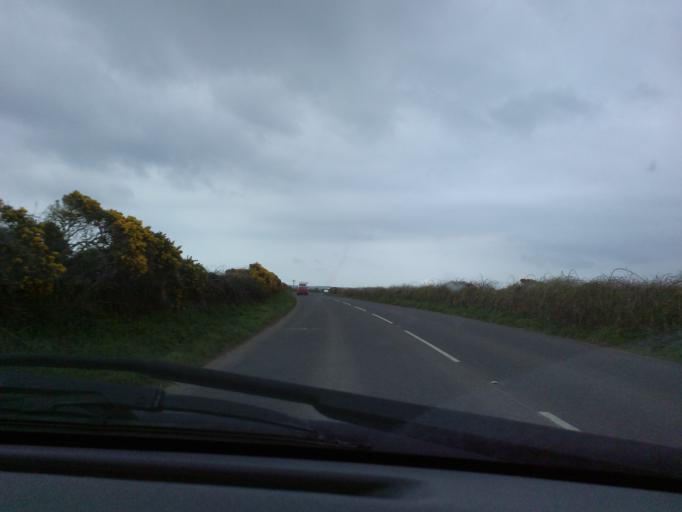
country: GB
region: England
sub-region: Cornwall
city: Sennen
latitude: 50.0810
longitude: -5.6812
